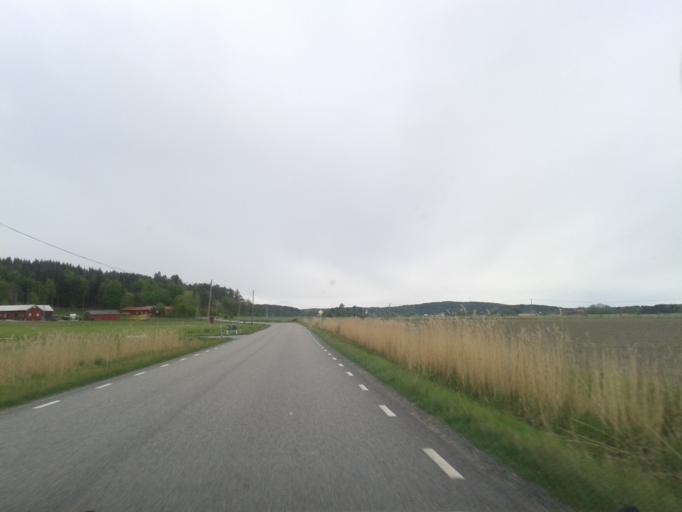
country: SE
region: Vaestra Goetaland
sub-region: Kungalvs Kommun
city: Kode
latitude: 57.9641
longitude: 11.8213
